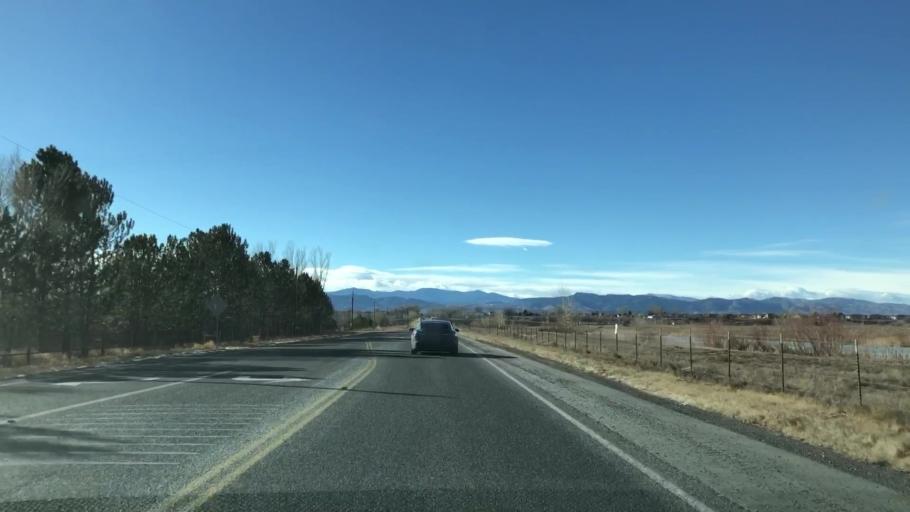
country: US
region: Colorado
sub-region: Weld County
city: Windsor
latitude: 40.5085
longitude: -104.9827
